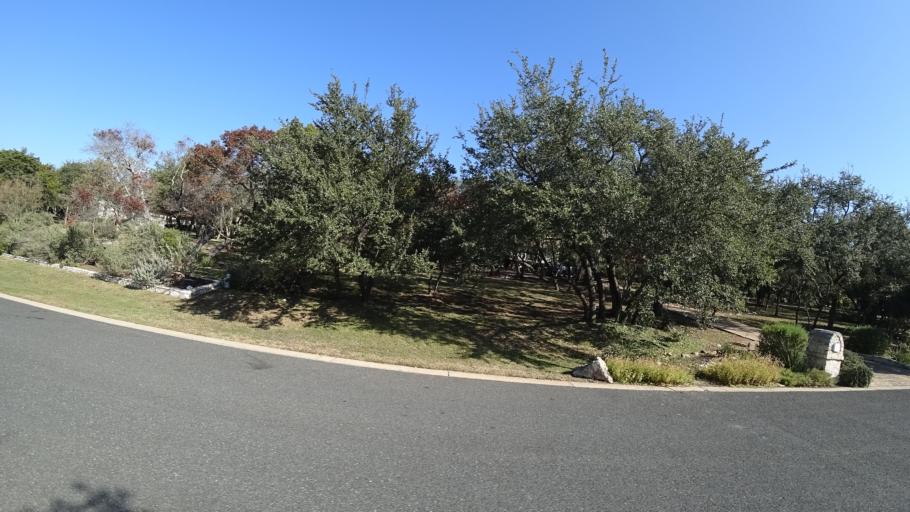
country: US
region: Texas
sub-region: Williamson County
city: Anderson Mill
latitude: 30.3813
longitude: -97.8308
